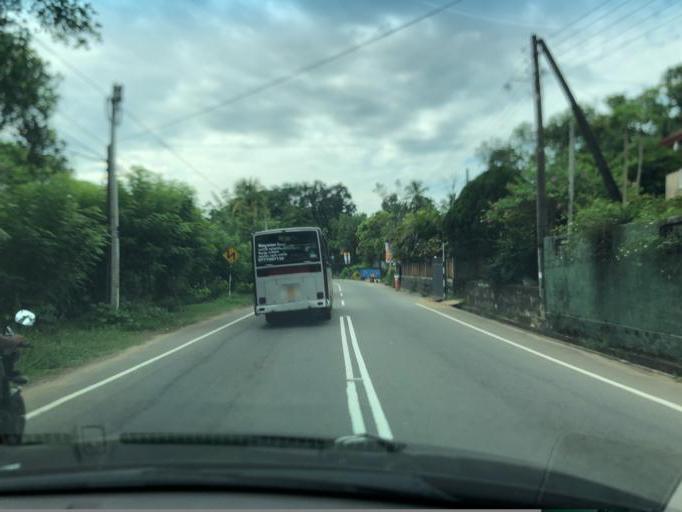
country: LK
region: Western
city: Beruwala
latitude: 6.5438
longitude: 80.0382
